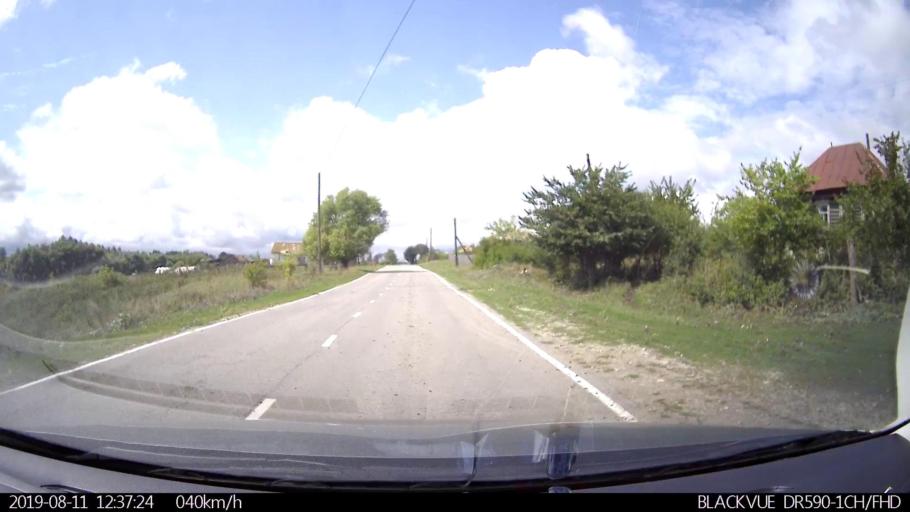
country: RU
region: Ulyanovsk
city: Ignatovka
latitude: 53.8239
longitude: 47.8156
